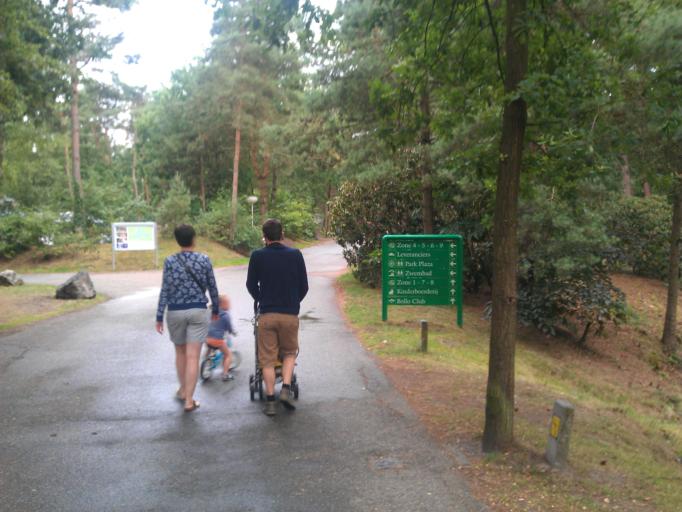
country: NL
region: North Brabant
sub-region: Gemeente Bladel en Netersel
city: Bladel
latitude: 51.3416
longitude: 5.2485
